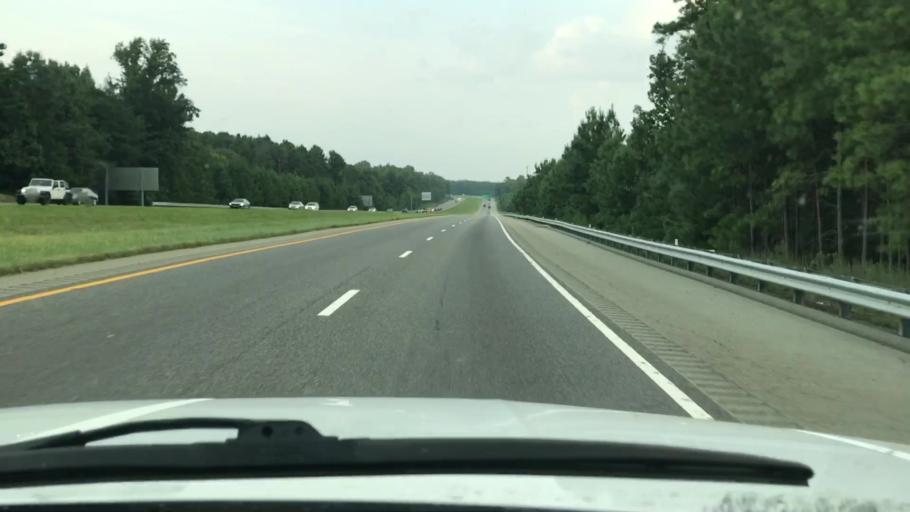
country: US
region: Virginia
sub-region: Chesterfield County
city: Brandermill
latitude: 37.5346
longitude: -77.6965
